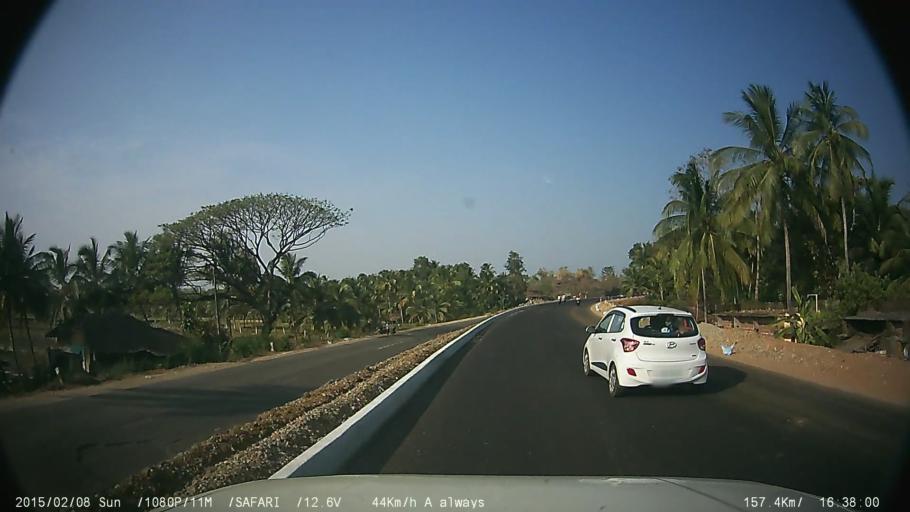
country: IN
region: Kerala
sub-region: Palakkad district
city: Palakkad
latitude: 10.6859
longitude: 76.5801
